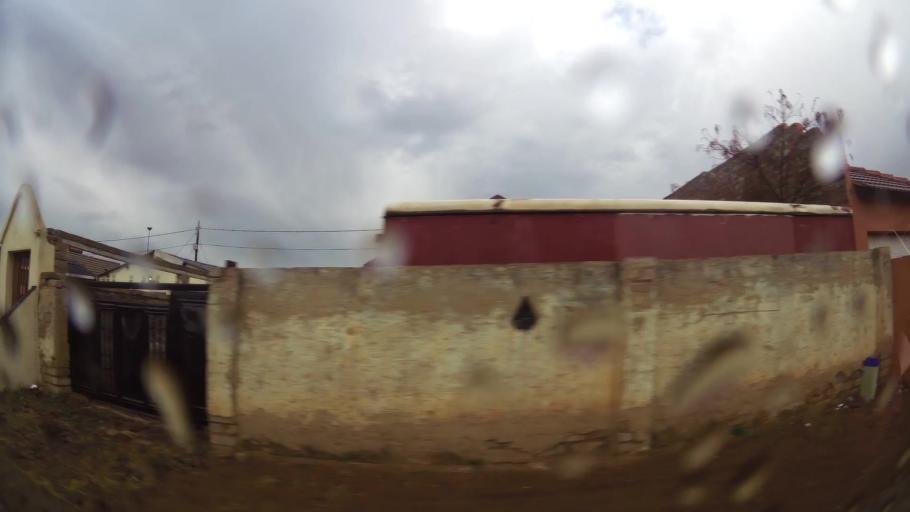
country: ZA
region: Gauteng
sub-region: Ekurhuleni Metropolitan Municipality
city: Germiston
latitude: -26.3413
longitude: 28.2028
